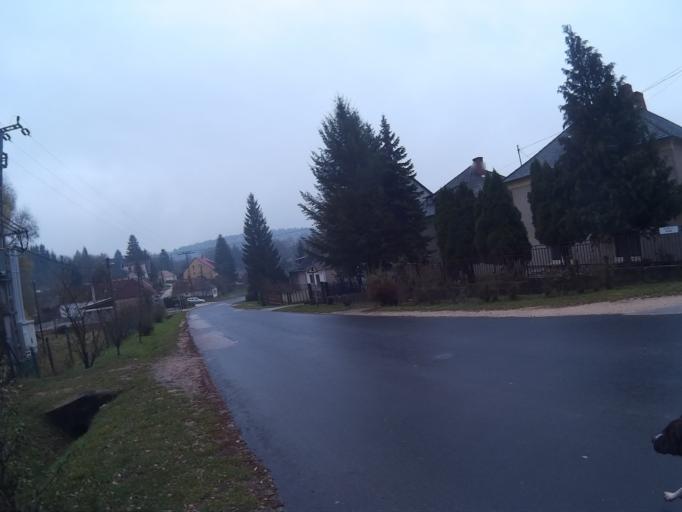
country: HU
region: Veszprem
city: Herend
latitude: 47.2546
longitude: 17.7321
